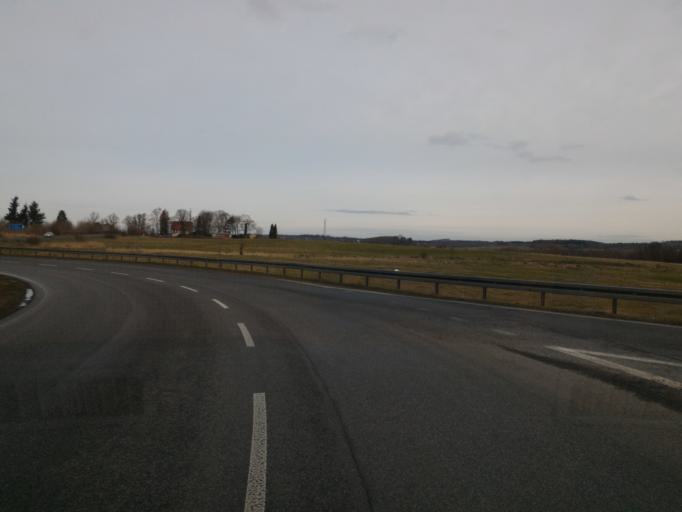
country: CZ
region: Ustecky
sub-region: Okres Decin
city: Rumburk
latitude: 50.9379
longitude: 14.5590
